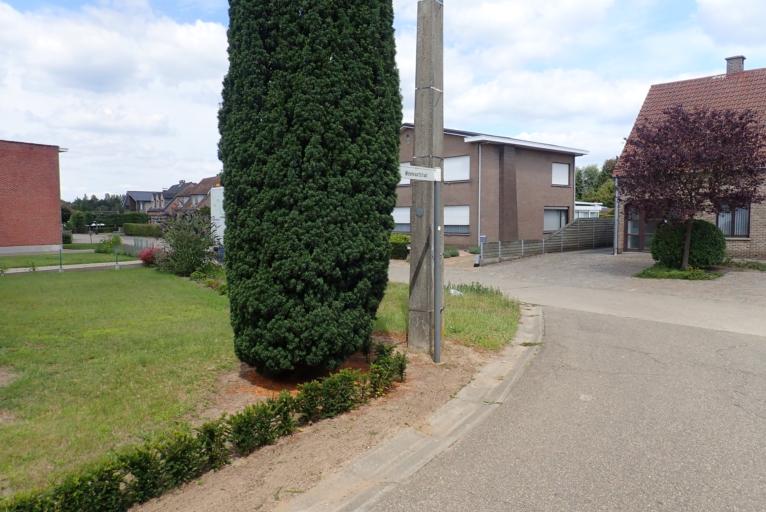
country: BE
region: Flanders
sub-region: Provincie Antwerpen
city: Nijlen
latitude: 51.1707
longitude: 4.6492
